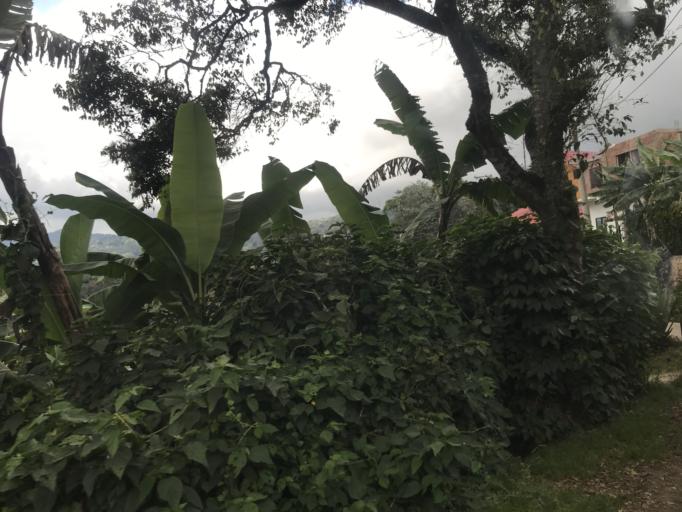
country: CO
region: Valle del Cauca
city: Cali
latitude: 3.5188
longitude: -76.6059
